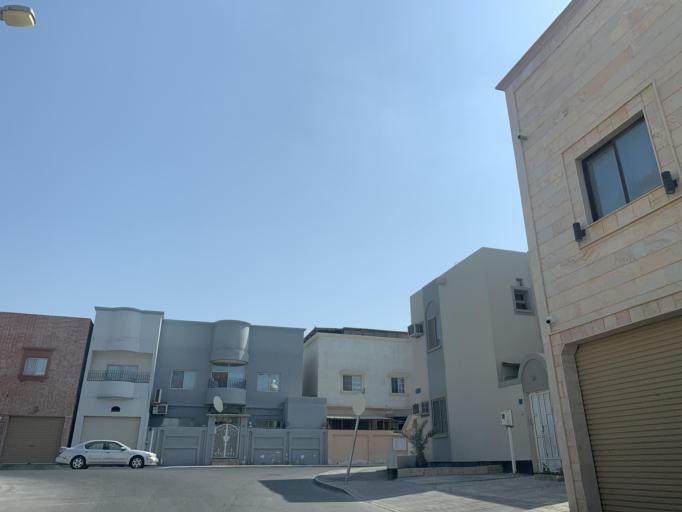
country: BH
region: Central Governorate
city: Madinat Hamad
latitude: 26.1314
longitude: 50.5015
